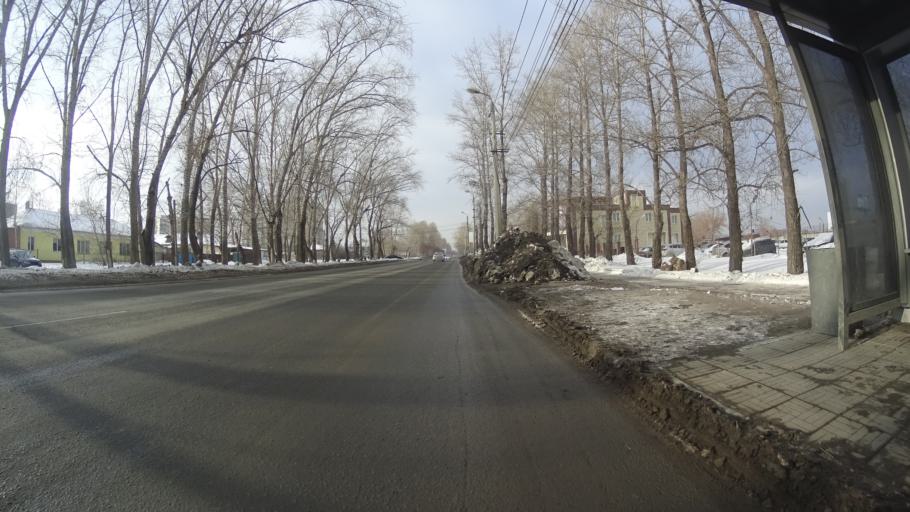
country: RU
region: Chelyabinsk
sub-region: Gorod Chelyabinsk
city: Chelyabinsk
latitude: 55.1217
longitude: 61.3774
